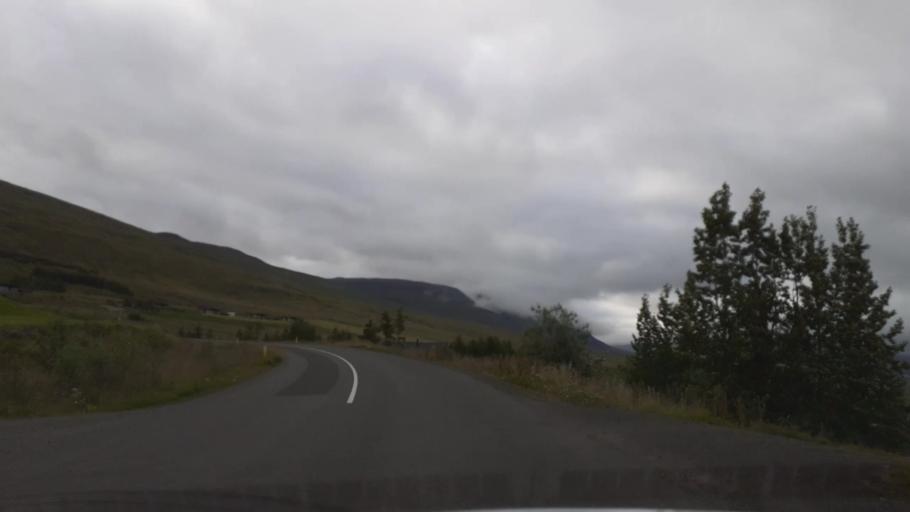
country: IS
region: Northeast
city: Akureyri
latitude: 65.6801
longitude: -18.0410
